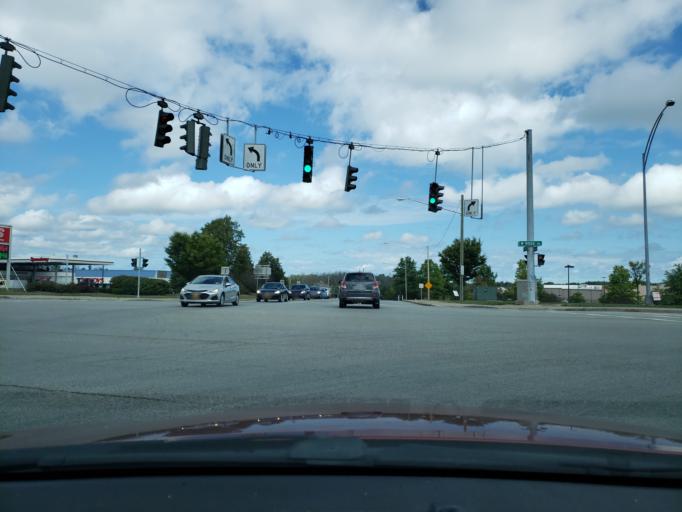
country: US
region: New York
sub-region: Monroe County
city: Greece
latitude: 43.2143
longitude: -77.7318
